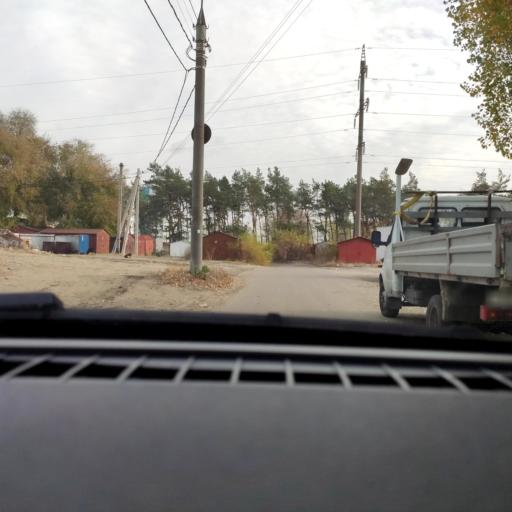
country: RU
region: Voronezj
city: Maslovka
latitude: 51.6345
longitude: 39.2878
